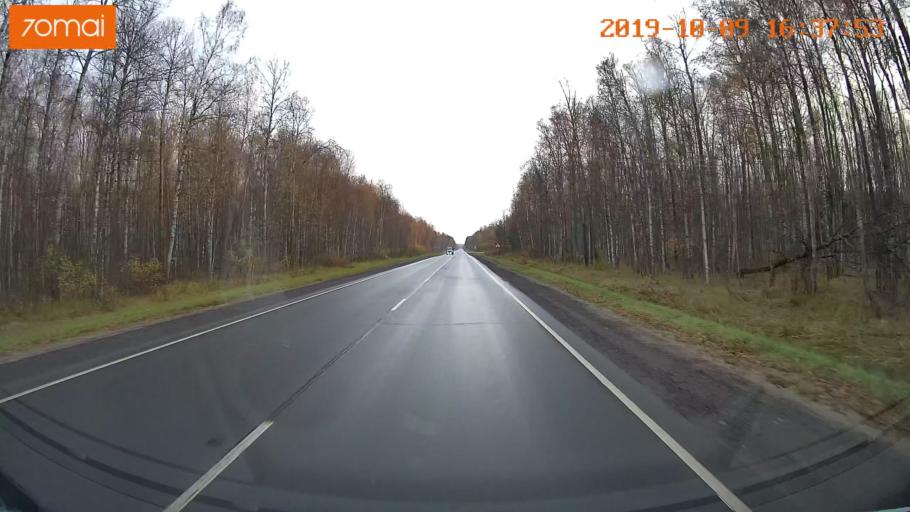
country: RU
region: Kostroma
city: Volgorechensk
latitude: 57.5203
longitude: 41.0302
